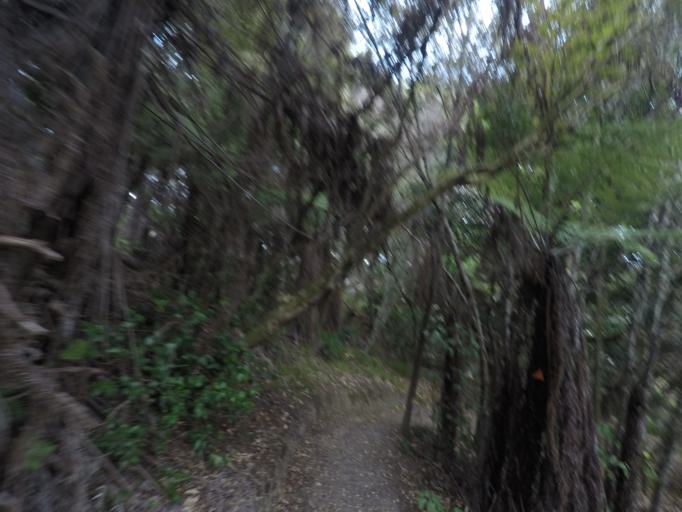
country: NZ
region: Auckland
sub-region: Auckland
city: Rothesay Bay
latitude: -36.6493
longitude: 174.7272
